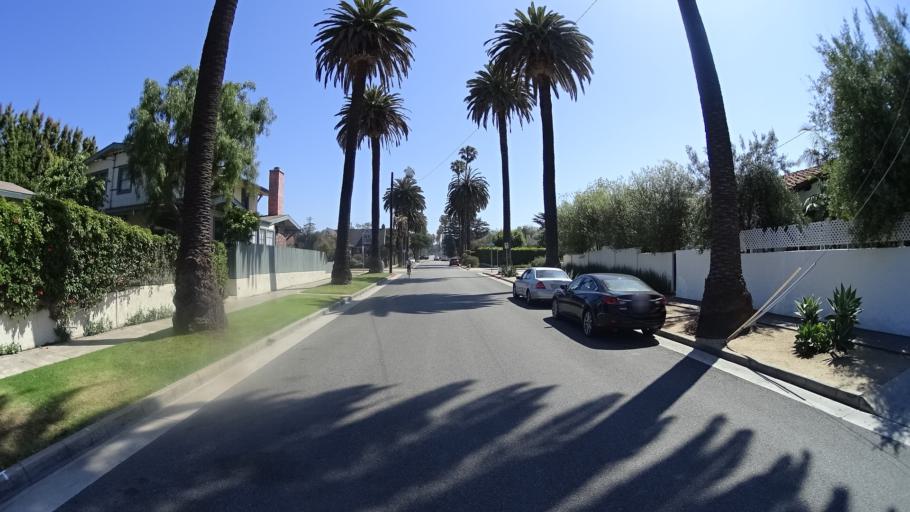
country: US
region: California
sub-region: Los Angeles County
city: Santa Monica
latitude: 34.0318
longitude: -118.5030
